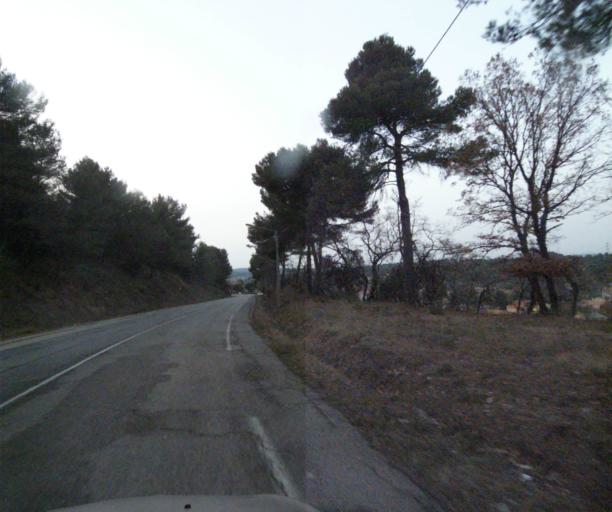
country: FR
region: Provence-Alpes-Cote d'Azur
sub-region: Departement des Bouches-du-Rhone
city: Gardanne
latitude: 43.4256
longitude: 5.4769
